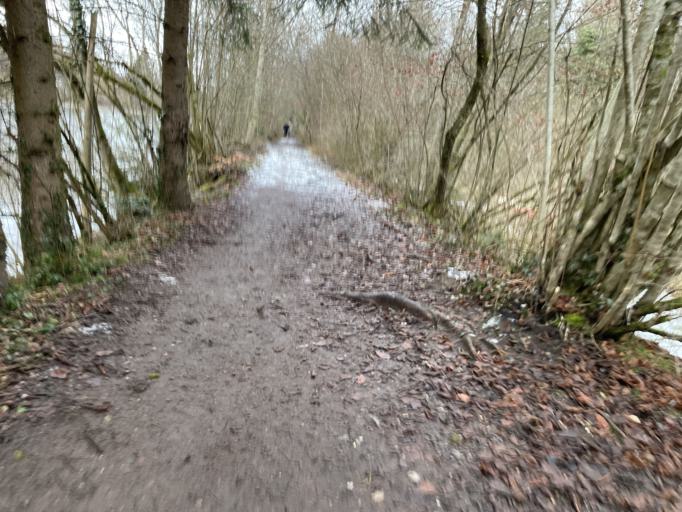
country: CH
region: Bern
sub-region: Thun District
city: Uttigen
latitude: 46.8114
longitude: 7.5699
